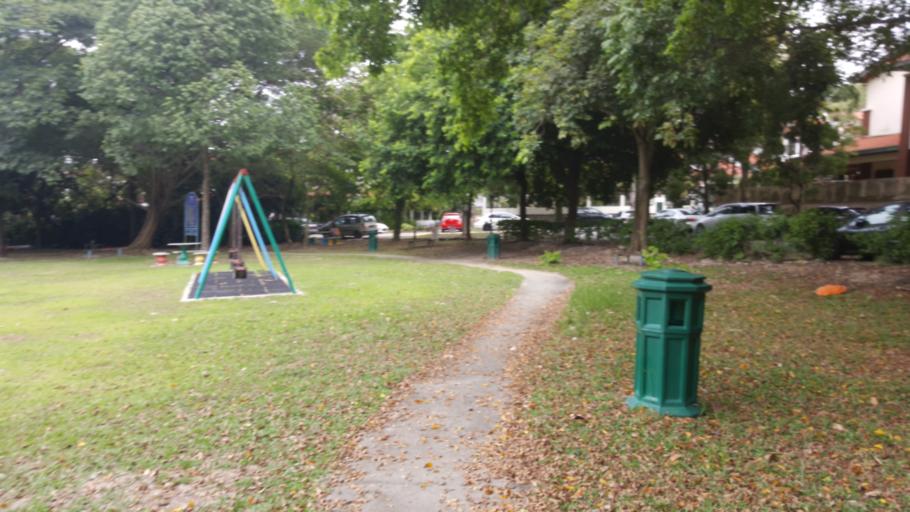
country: MY
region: Selangor
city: Kampung Baru Subang
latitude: 3.1456
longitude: 101.5766
